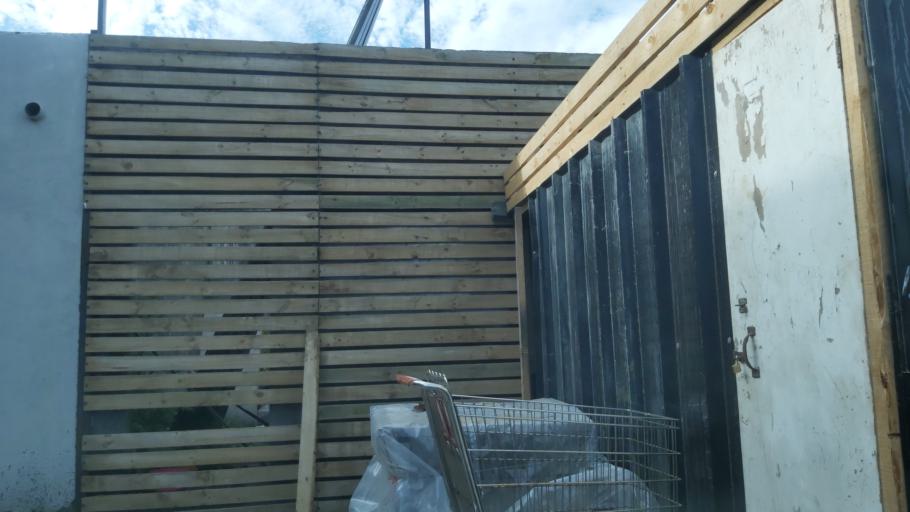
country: CL
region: Maule
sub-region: Provincia de Cauquenes
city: Cauquenes
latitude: -36.1341
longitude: -72.7993
